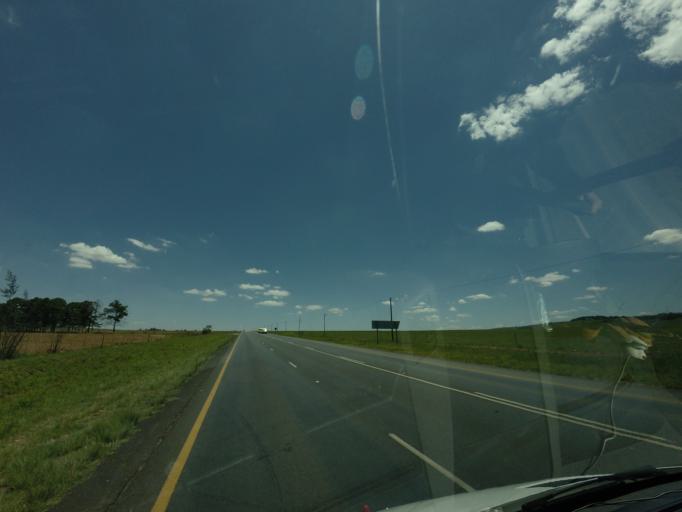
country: ZA
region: Mpumalanga
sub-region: Nkangala District Municipality
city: Belfast
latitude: -25.6944
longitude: 30.2051
